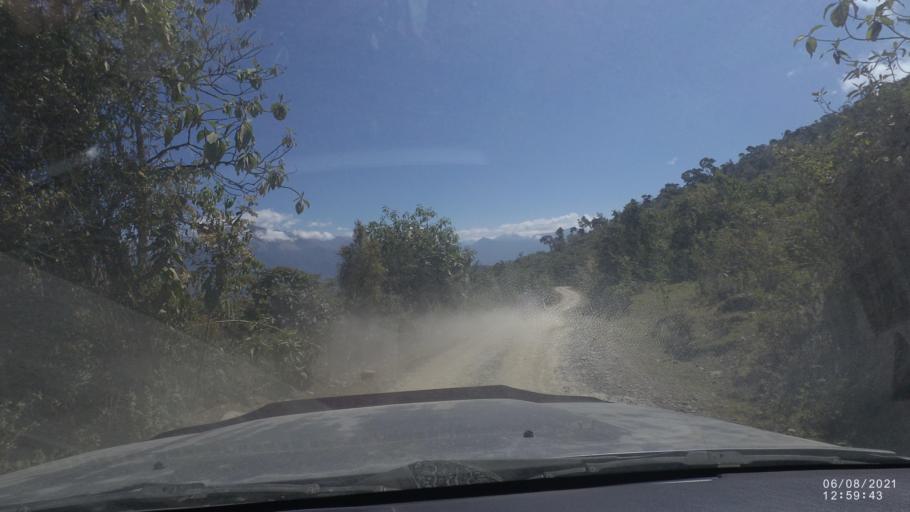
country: BO
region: Cochabamba
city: Colchani
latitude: -16.7496
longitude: -66.6874
